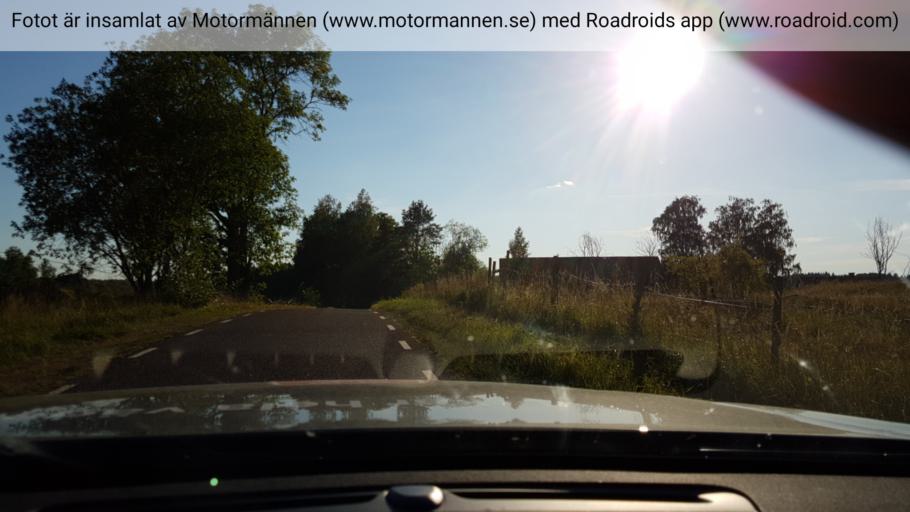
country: SE
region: Vaestmanland
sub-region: Surahammars Kommun
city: Surahammar
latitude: 59.6752
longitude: 16.0782
